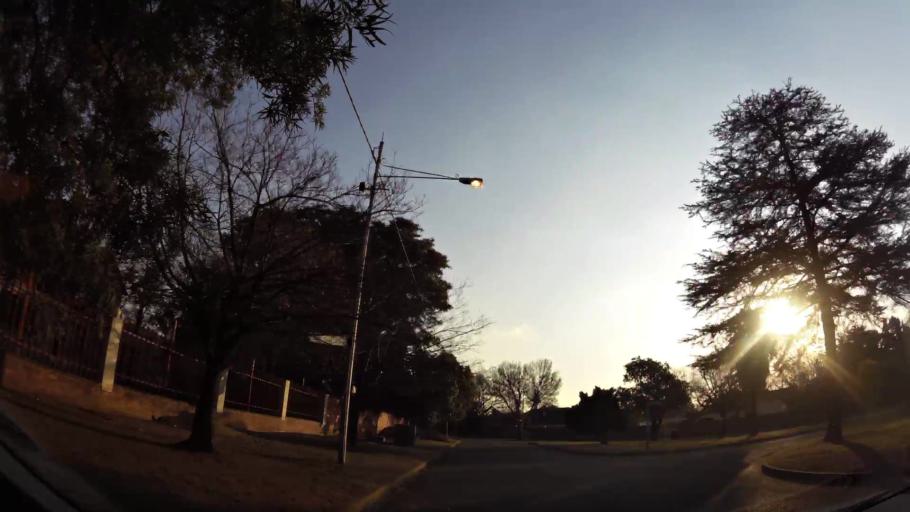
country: ZA
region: Gauteng
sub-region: Ekurhuleni Metropolitan Municipality
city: Springs
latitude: -26.3028
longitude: 28.4490
